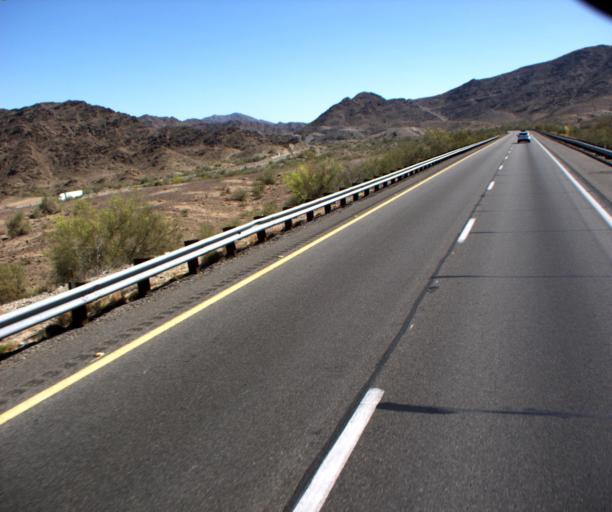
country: US
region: Arizona
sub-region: La Paz County
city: Ehrenberg
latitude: 33.6327
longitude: -114.3995
